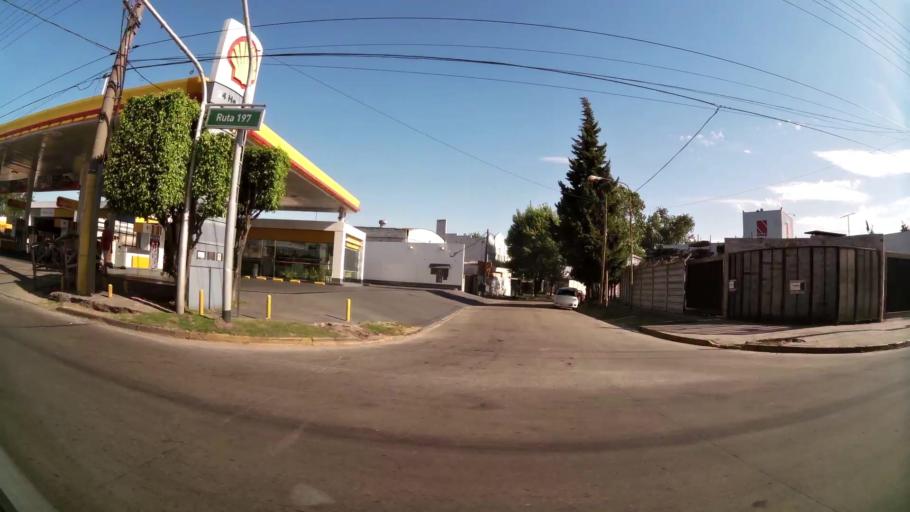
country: AR
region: Buenos Aires
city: Santa Catalina - Dique Lujan
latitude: -34.4785
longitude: -58.6721
